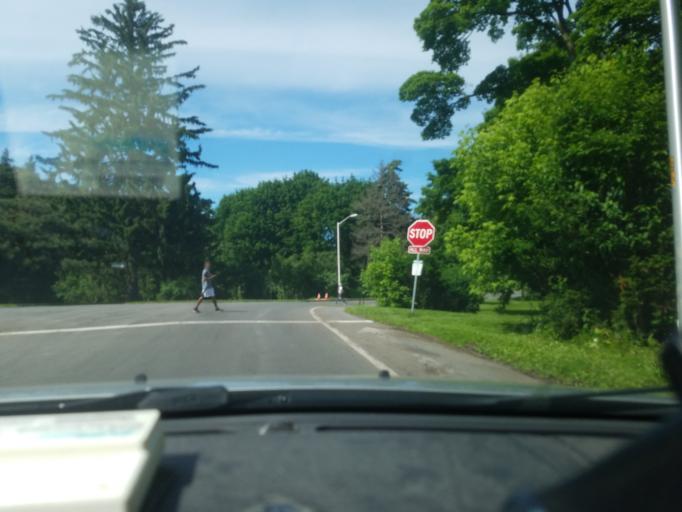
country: US
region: New York
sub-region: Onondaga County
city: Syracuse
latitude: 43.0432
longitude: -76.1255
